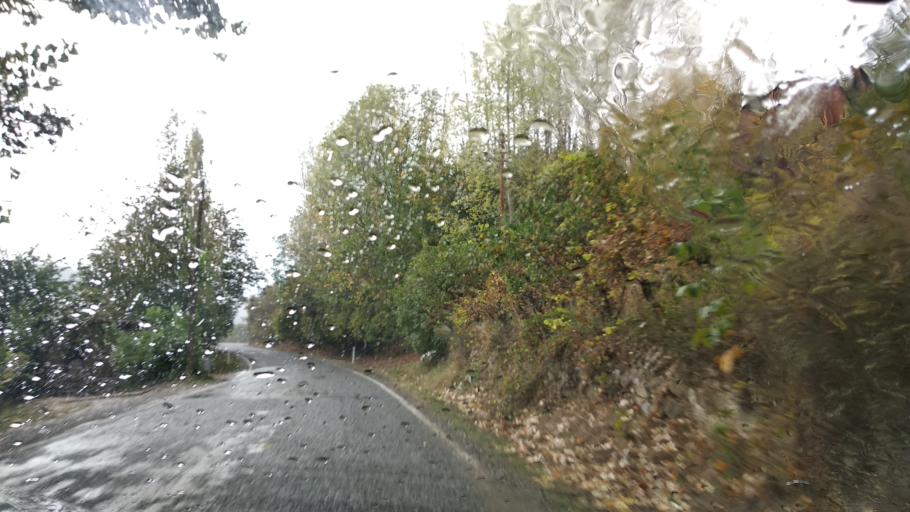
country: TR
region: Ankara
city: Nallihan
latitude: 40.3295
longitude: 31.4109
